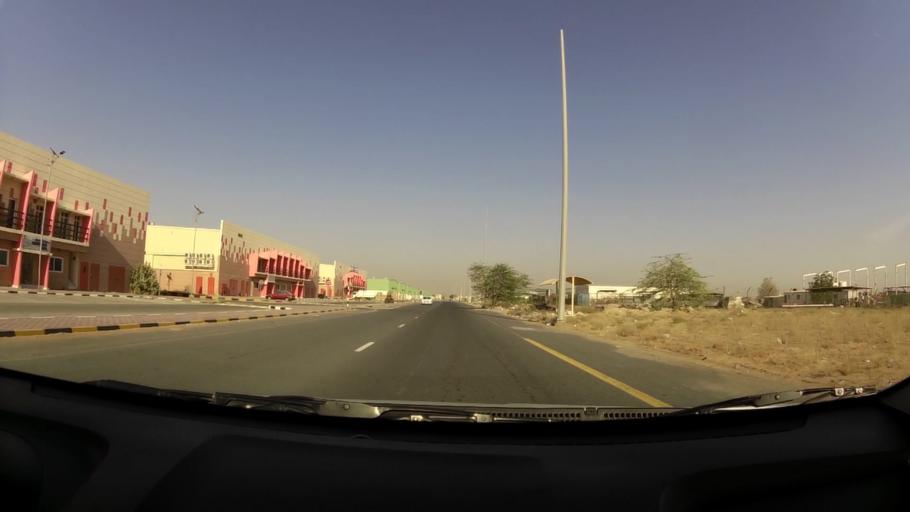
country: AE
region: Umm al Qaywayn
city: Umm al Qaywayn
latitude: 25.4348
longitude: 55.5803
